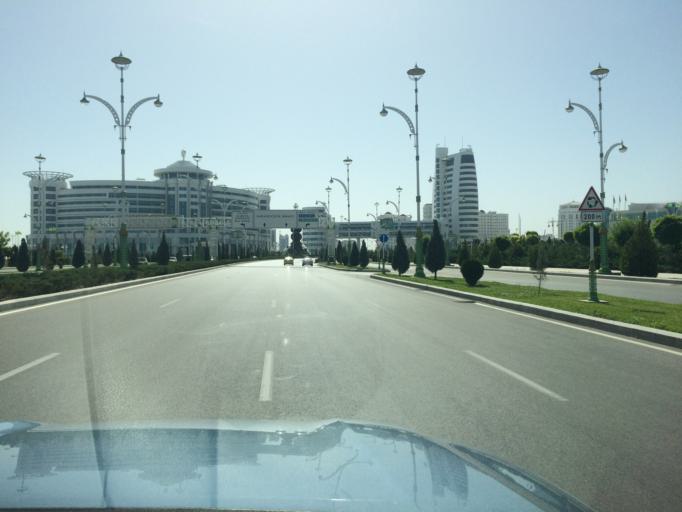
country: TM
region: Ahal
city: Ashgabat
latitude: 37.8976
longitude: 58.3670
